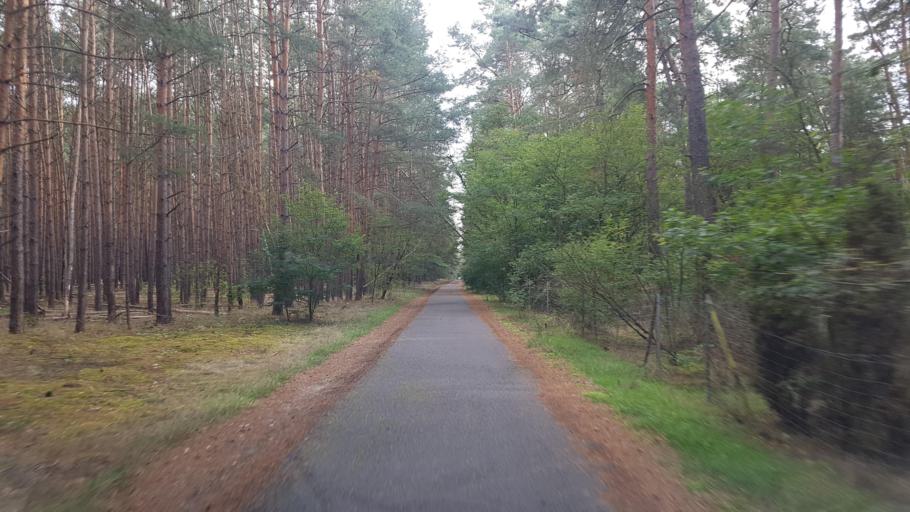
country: DE
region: Brandenburg
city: Ihlow
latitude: 51.8678
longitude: 13.2542
